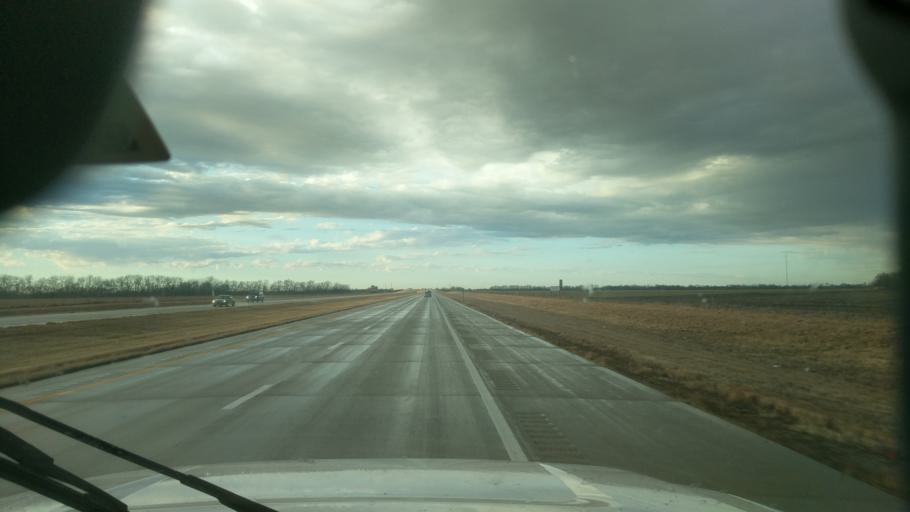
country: US
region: Kansas
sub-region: Harvey County
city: North Newton
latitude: 38.0941
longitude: -97.3625
